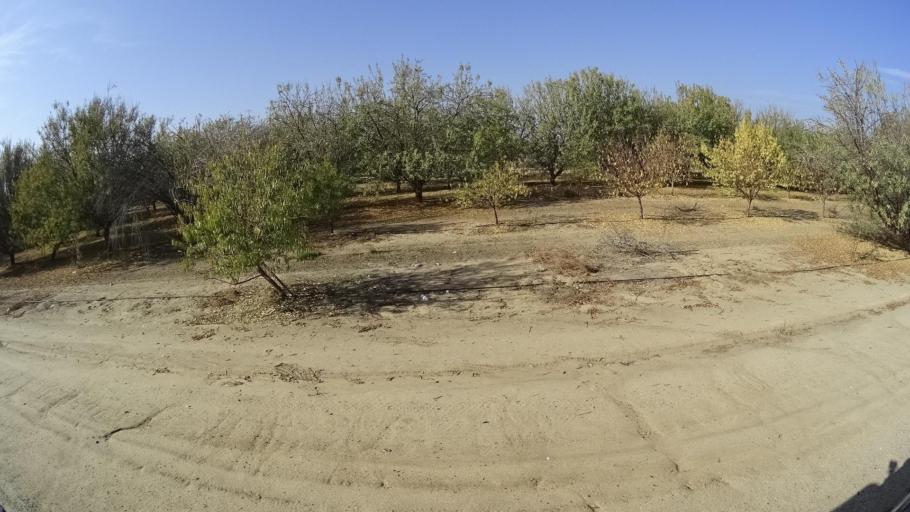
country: US
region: California
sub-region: Kern County
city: McFarland
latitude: 35.6912
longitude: -119.2231
